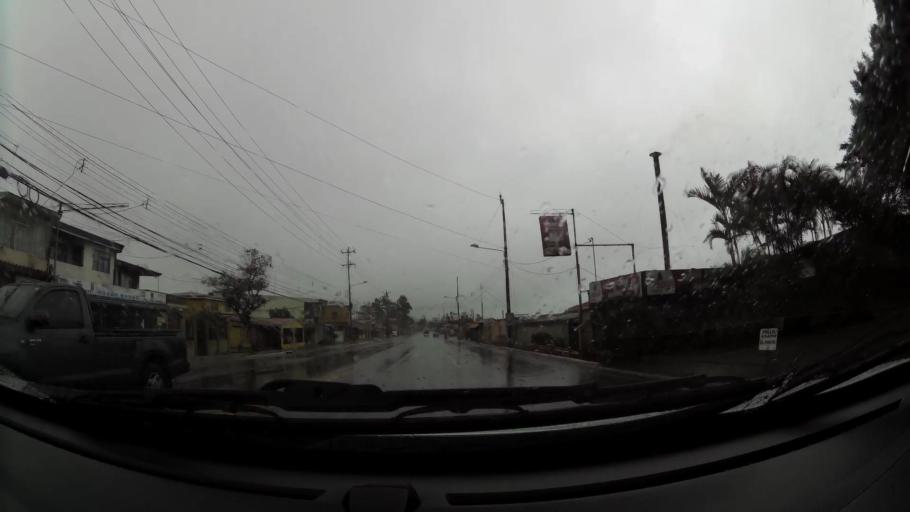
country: CR
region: Cartago
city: Cartago
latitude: 9.8618
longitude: -83.9121
